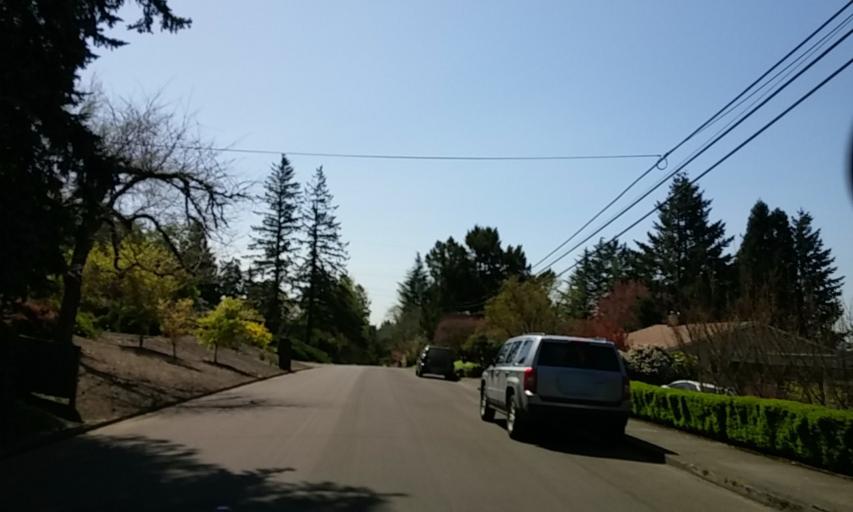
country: US
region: Oregon
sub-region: Washington County
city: West Haven
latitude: 45.5189
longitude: -122.7671
